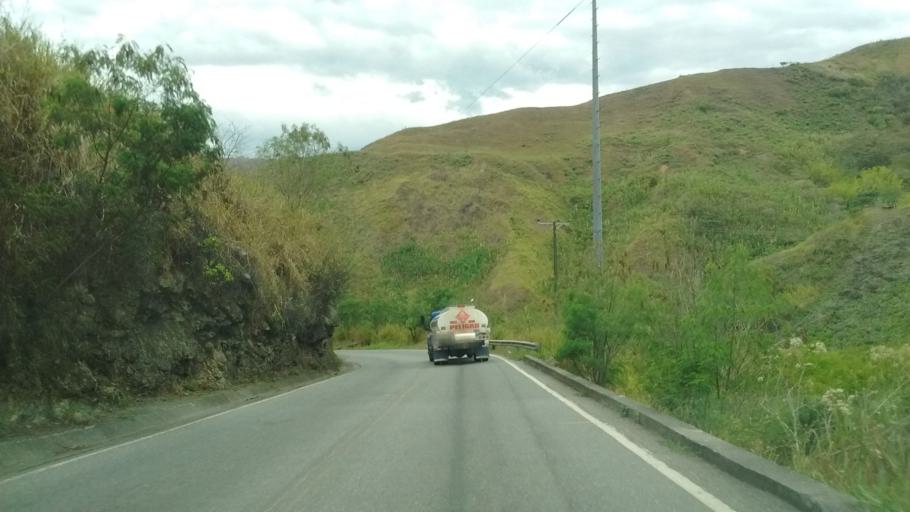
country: CO
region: Cauca
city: La Sierra
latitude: 2.1979
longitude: -76.8224
